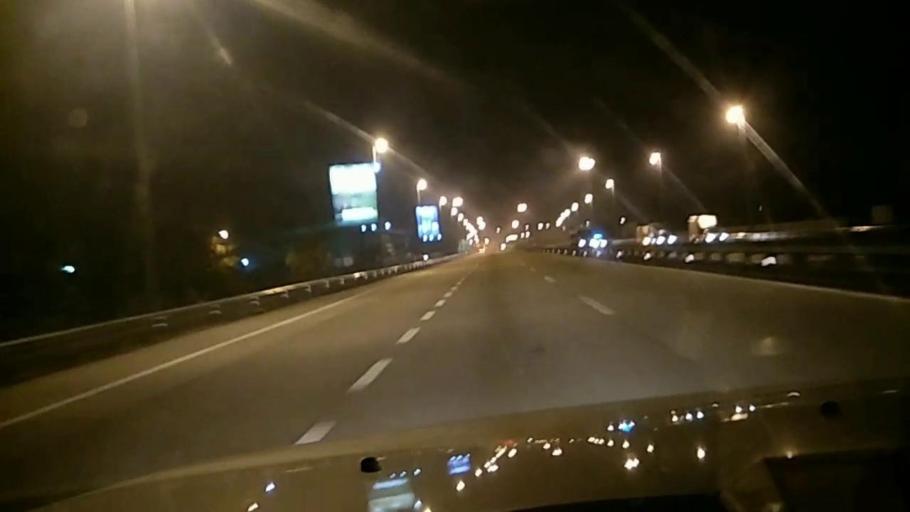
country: MY
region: Penang
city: Juru
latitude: 5.2451
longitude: 100.4741
